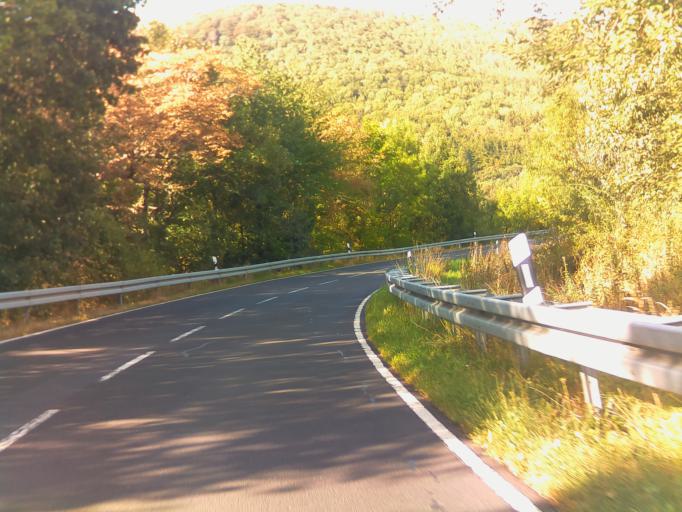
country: DE
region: Thuringia
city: Birx
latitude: 50.5199
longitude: 10.0353
